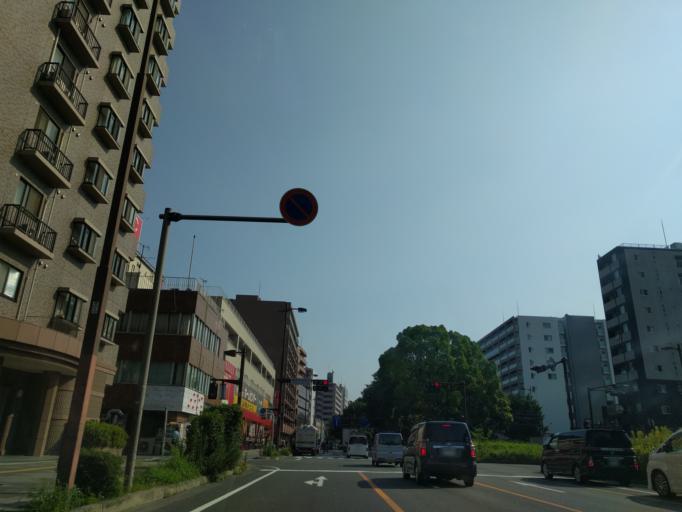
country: JP
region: Kanagawa
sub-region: Kawasaki-shi
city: Kawasaki
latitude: 35.5064
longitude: 139.6801
